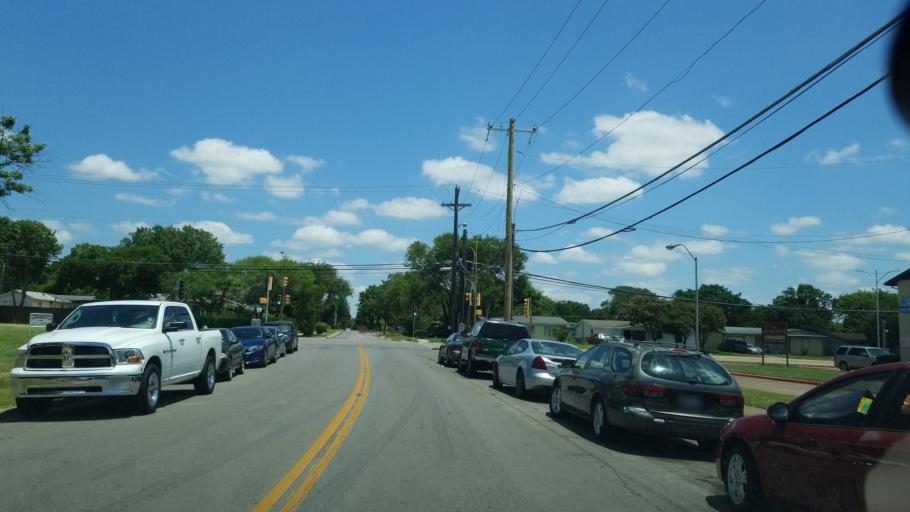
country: US
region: Texas
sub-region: Dallas County
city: Balch Springs
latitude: 32.7383
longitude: -96.7010
